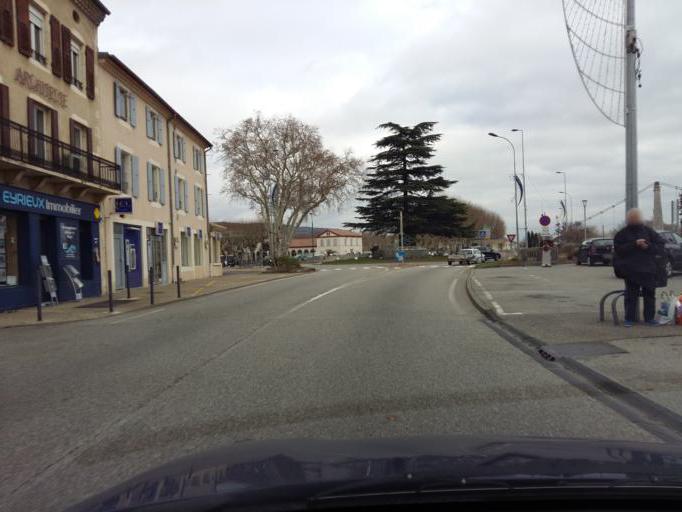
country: FR
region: Rhone-Alpes
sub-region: Departement de l'Ardeche
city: La Voulte-sur-Rhone
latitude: 44.7994
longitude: 4.7811
